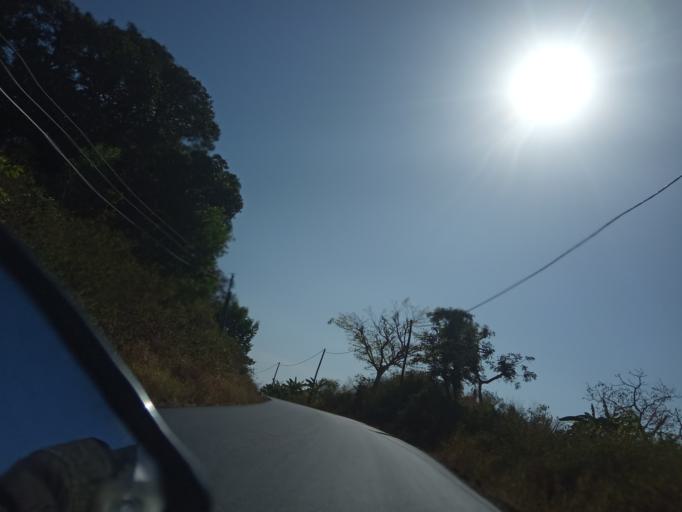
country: YT
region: Bandrele
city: Bandrele
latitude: -12.8916
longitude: 45.2083
